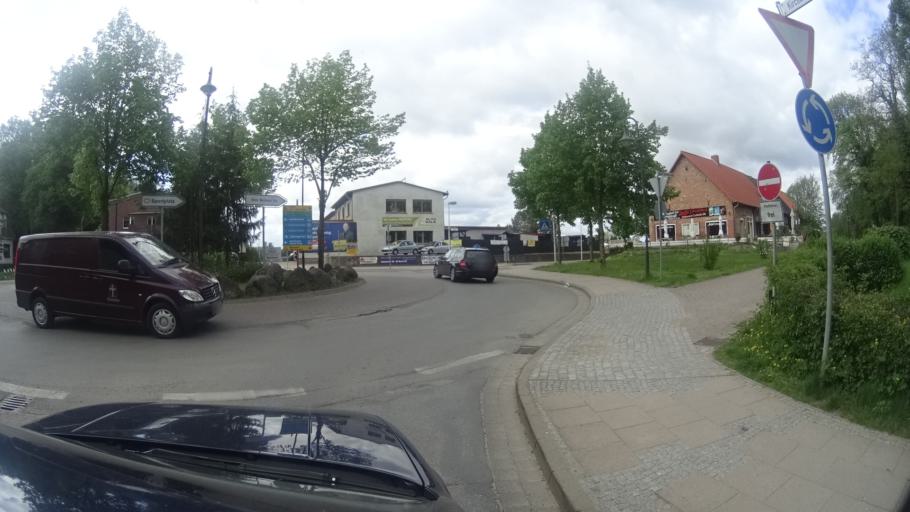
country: DE
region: Mecklenburg-Vorpommern
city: Malchow
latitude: 53.4756
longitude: 12.4221
